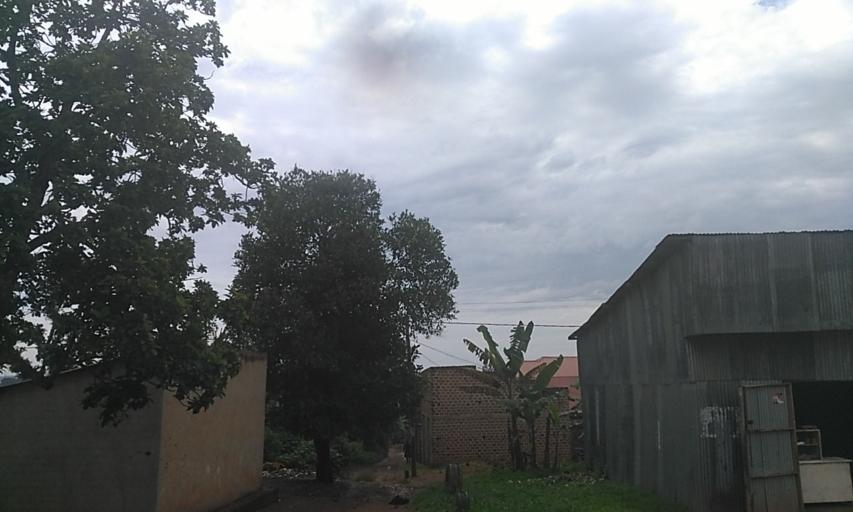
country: UG
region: Central Region
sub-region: Wakiso District
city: Bweyogerere
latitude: 0.3955
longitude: 32.6948
